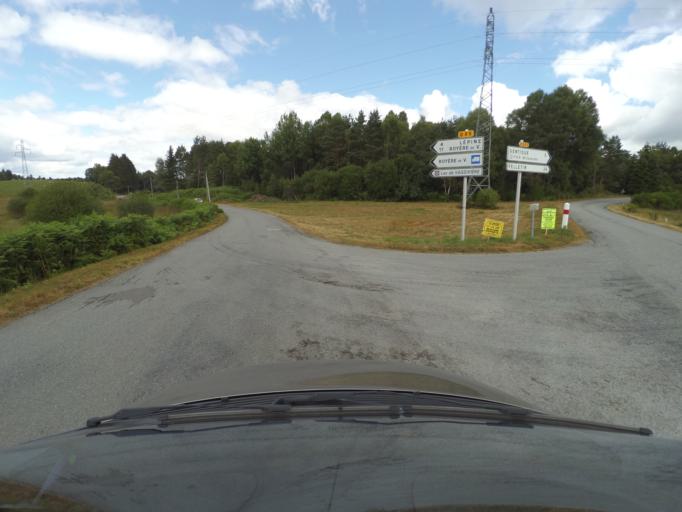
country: FR
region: Limousin
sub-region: Departement de la Creuse
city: Banize
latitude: 45.7588
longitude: 1.9541
